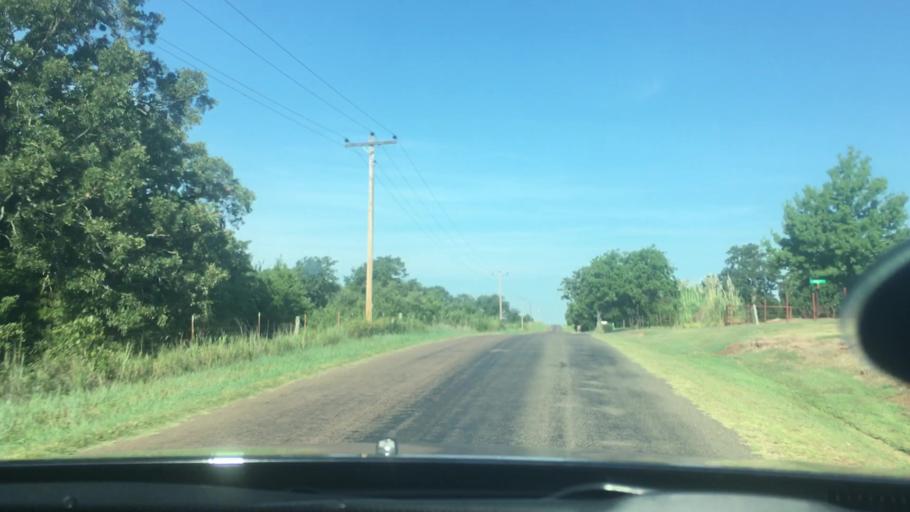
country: US
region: Oklahoma
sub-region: Garvin County
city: Pauls Valley
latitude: 34.6521
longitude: -97.3668
